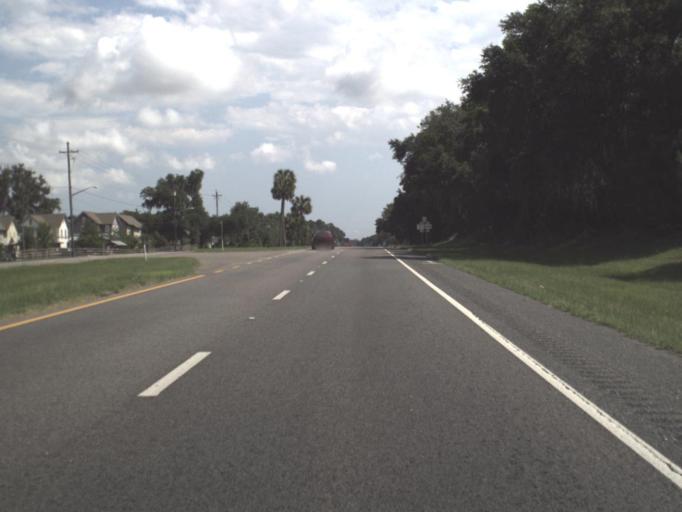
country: US
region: Florida
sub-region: Alachua County
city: Gainesville
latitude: 29.6079
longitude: -82.3418
